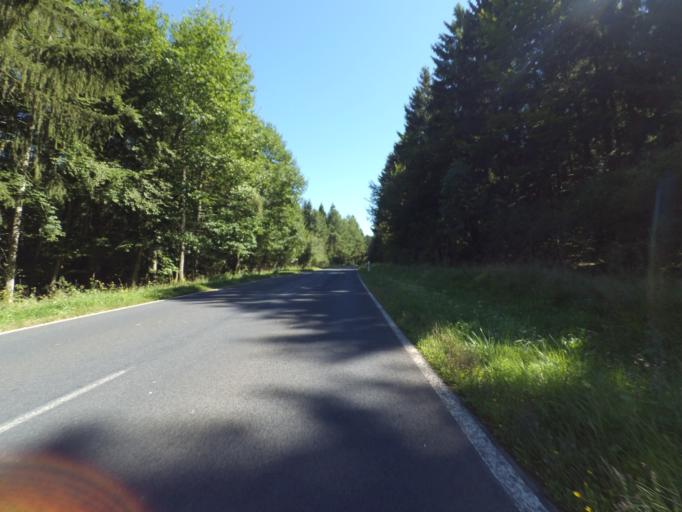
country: DE
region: Rheinland-Pfalz
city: Berndorf
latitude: 50.3333
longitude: 6.7044
